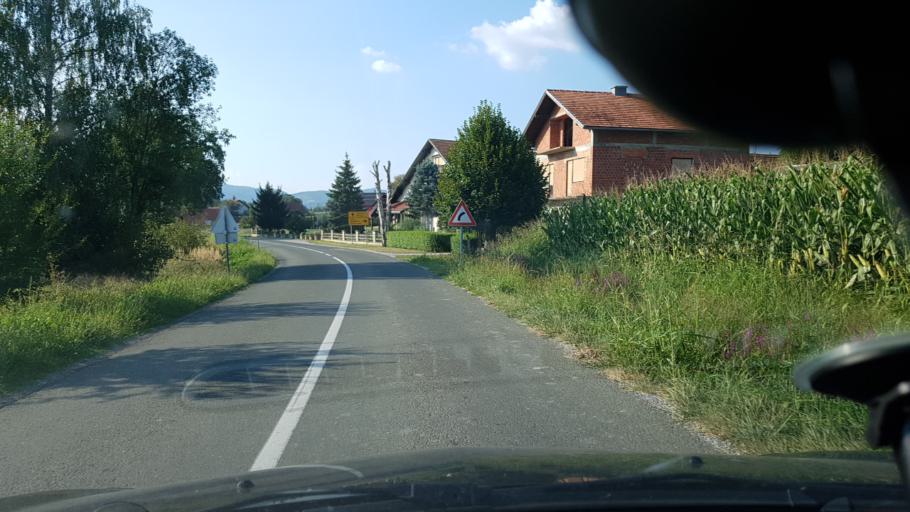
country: HR
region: Zagrebacka
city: Pojatno
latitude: 45.9746
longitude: 15.7370
